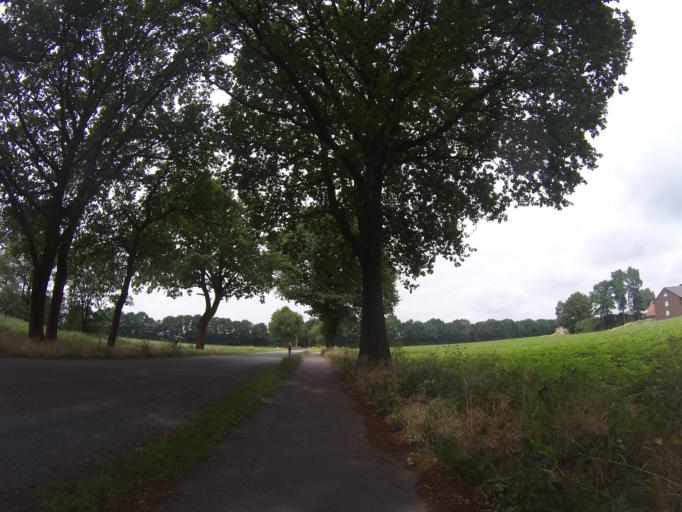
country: DE
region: Lower Saxony
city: Haren
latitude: 52.7066
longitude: 7.1820
